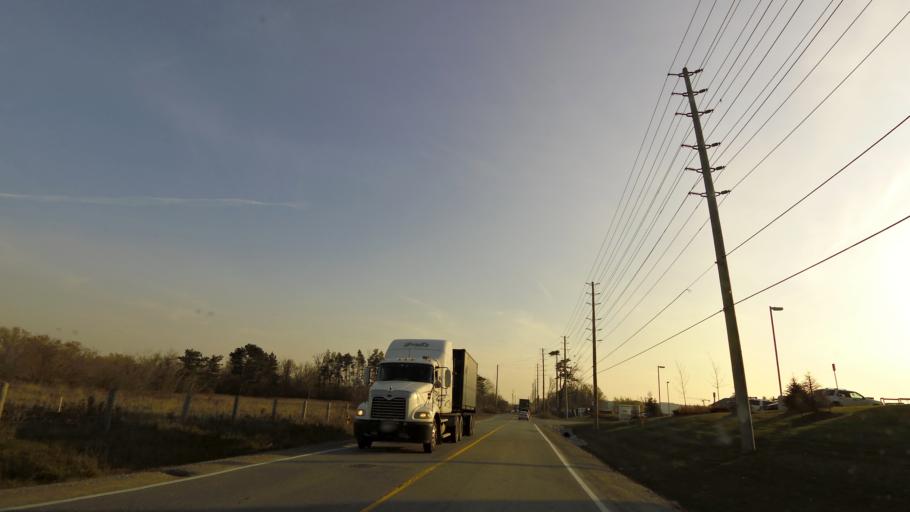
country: CA
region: Ontario
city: Vaughan
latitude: 43.7987
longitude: -79.6540
